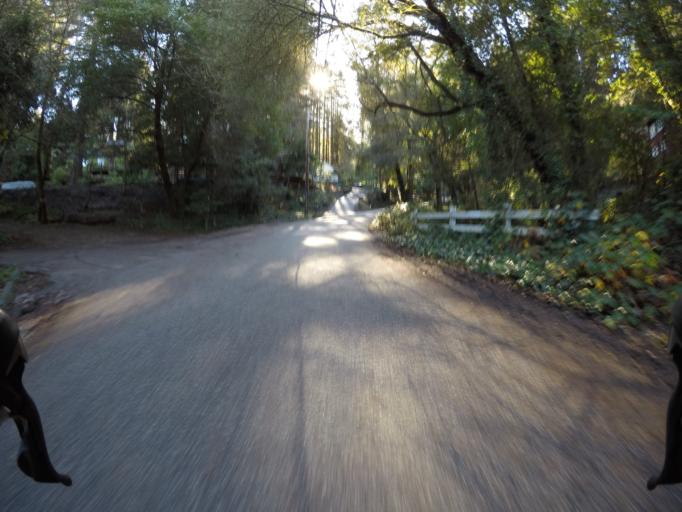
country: US
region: California
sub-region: Santa Cruz County
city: Felton
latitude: 37.0400
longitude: -122.0810
